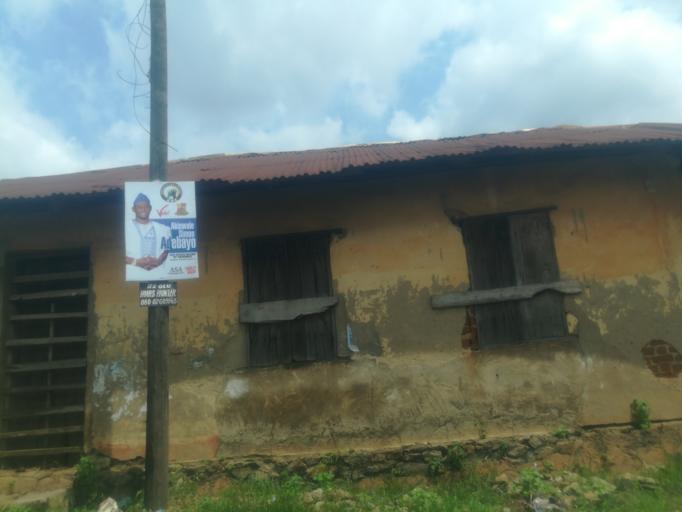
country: NG
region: Oyo
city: Ibadan
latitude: 7.3646
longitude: 3.8774
